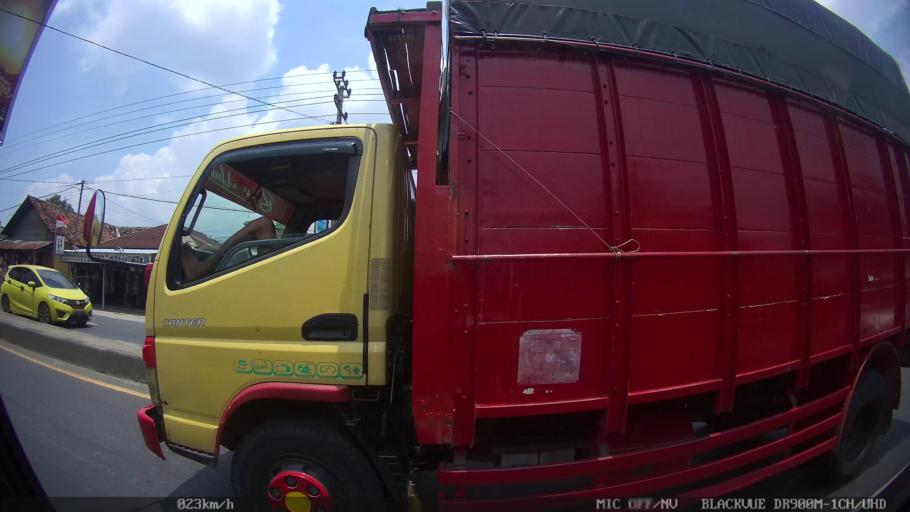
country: ID
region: Lampung
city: Natar
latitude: -5.3168
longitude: 105.1966
